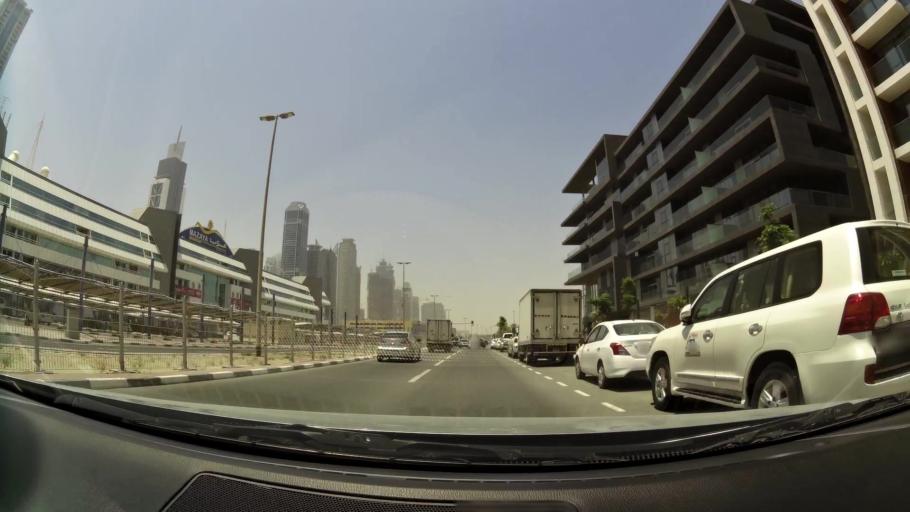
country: AE
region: Dubai
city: Dubai
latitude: 25.2003
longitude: 55.2652
